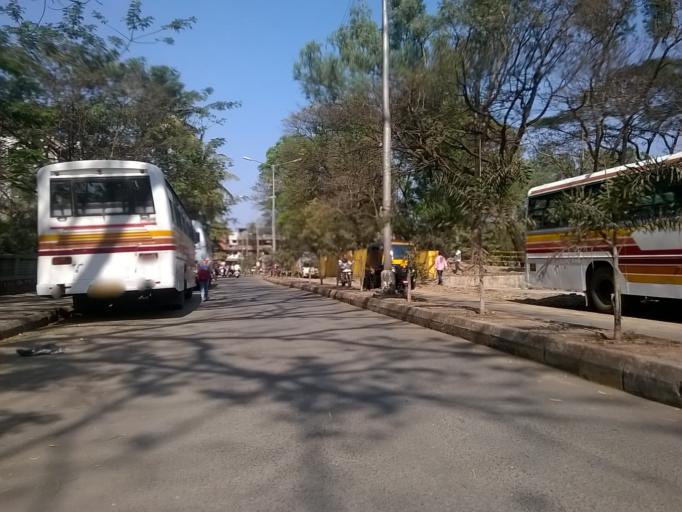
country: IN
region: Maharashtra
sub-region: Raigarh
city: Kalundri
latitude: 18.9938
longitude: 73.1264
